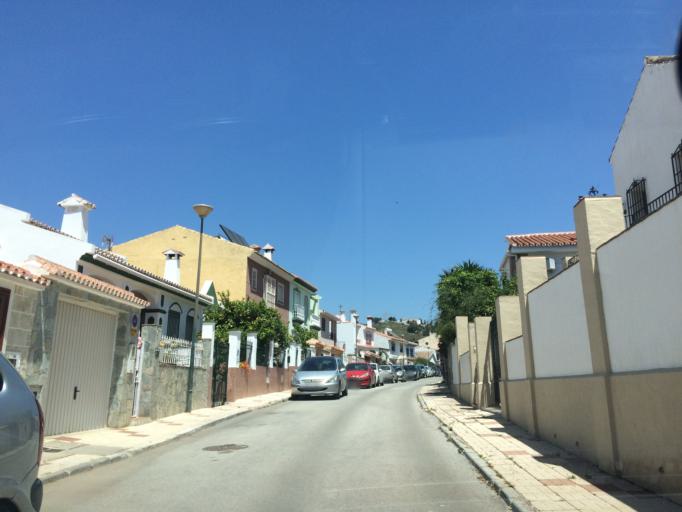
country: ES
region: Andalusia
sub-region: Provincia de Malaga
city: Malaga
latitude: 36.7308
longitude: -4.4815
